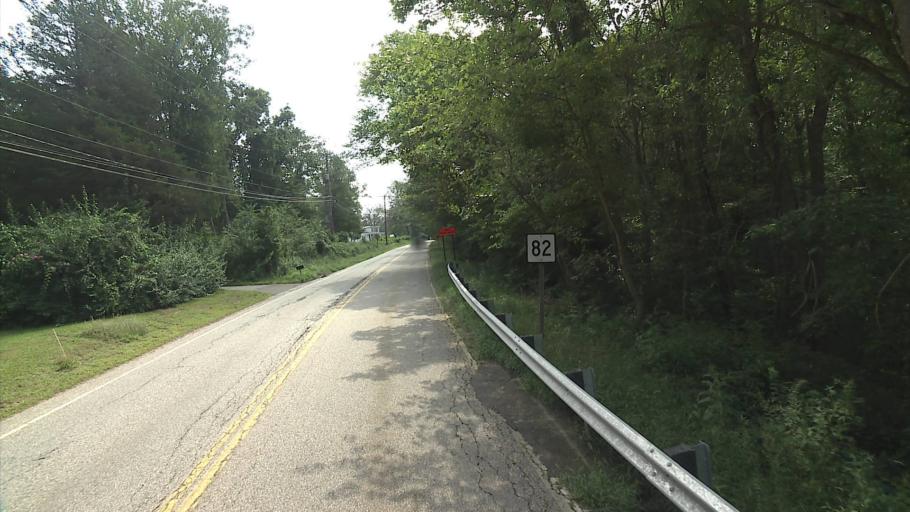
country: US
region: Connecticut
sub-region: Middlesex County
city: East Haddam
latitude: 41.4432
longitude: -72.4194
